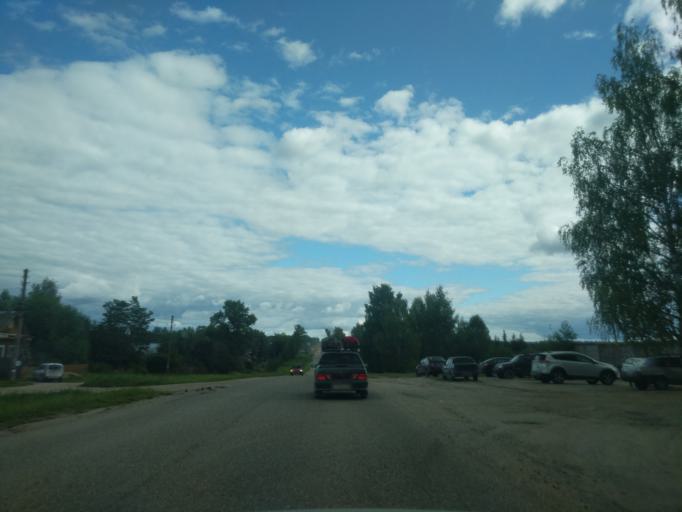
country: RU
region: Kostroma
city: Sudislavl'
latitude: 57.8802
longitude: 41.7204
